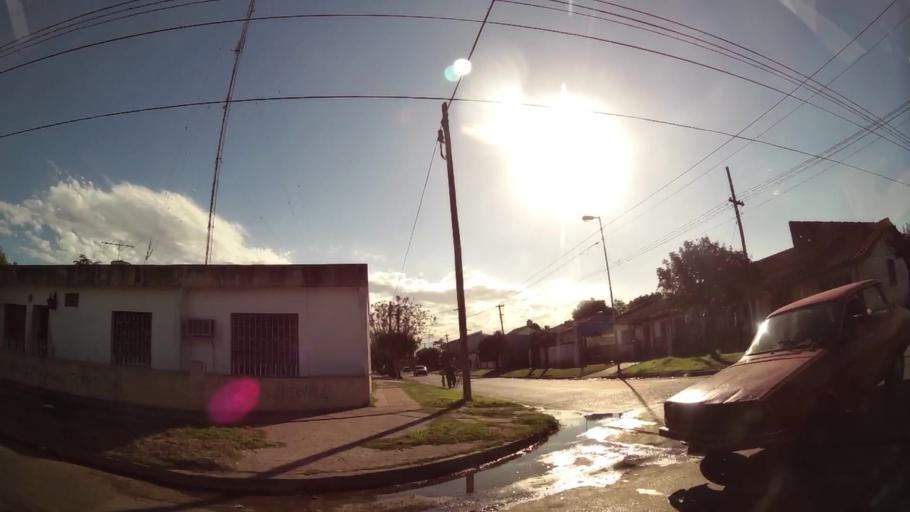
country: AR
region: Buenos Aires
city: Santa Catalina - Dique Lujan
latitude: -34.4903
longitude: -58.7292
